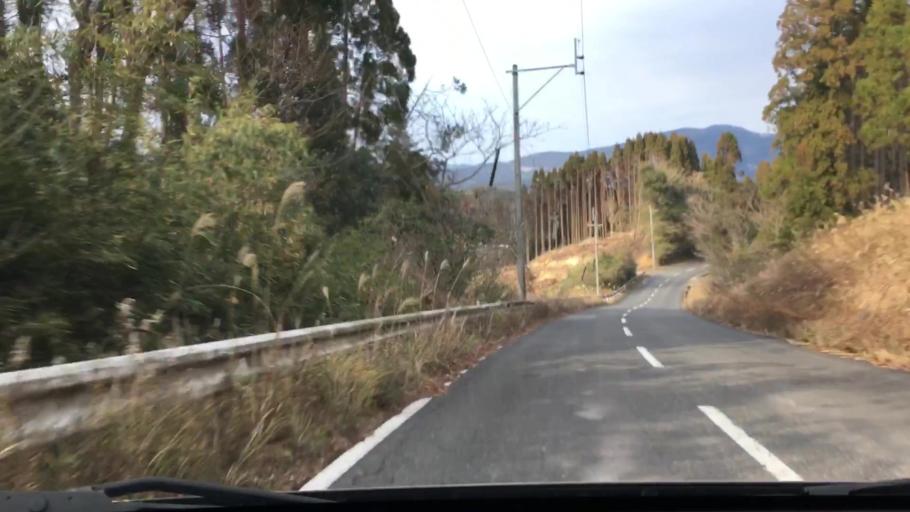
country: JP
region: Miyazaki
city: Nichinan
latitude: 31.6082
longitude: 131.3297
